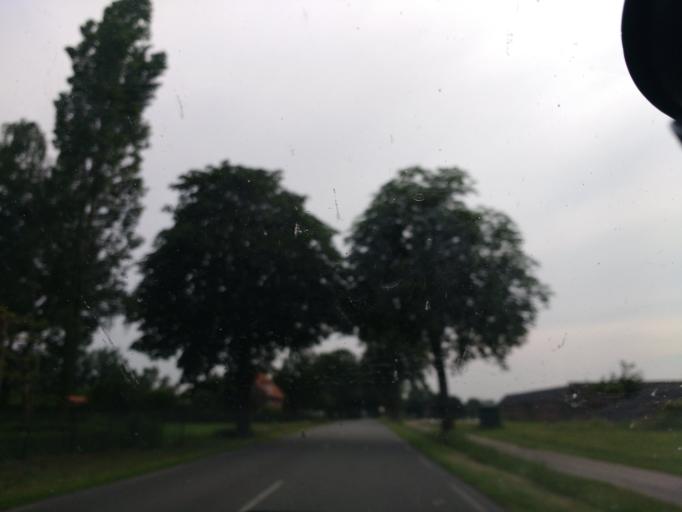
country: NL
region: North Brabant
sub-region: Gemeente Boxmeer
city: Overloon
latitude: 51.5821
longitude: 5.9728
